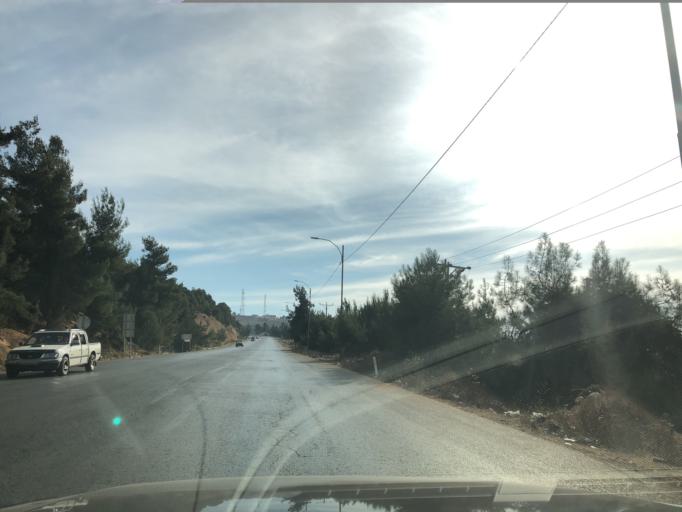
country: JO
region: Irbid
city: `Anjarah
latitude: 32.3089
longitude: 35.7778
